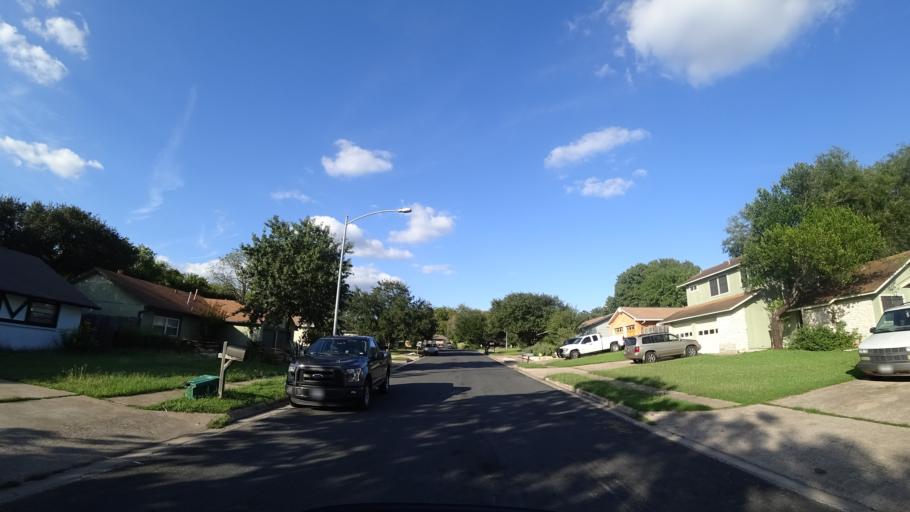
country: US
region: Texas
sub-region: Travis County
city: Onion Creek
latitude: 30.1968
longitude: -97.7976
